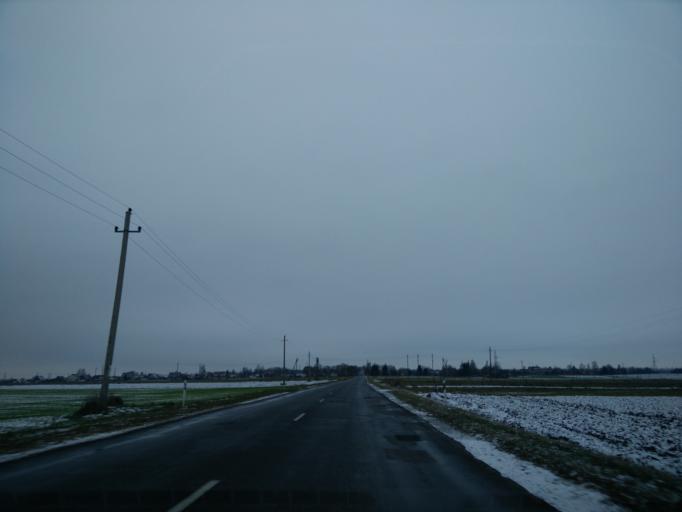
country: LT
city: Ariogala
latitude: 55.3539
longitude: 23.3793
